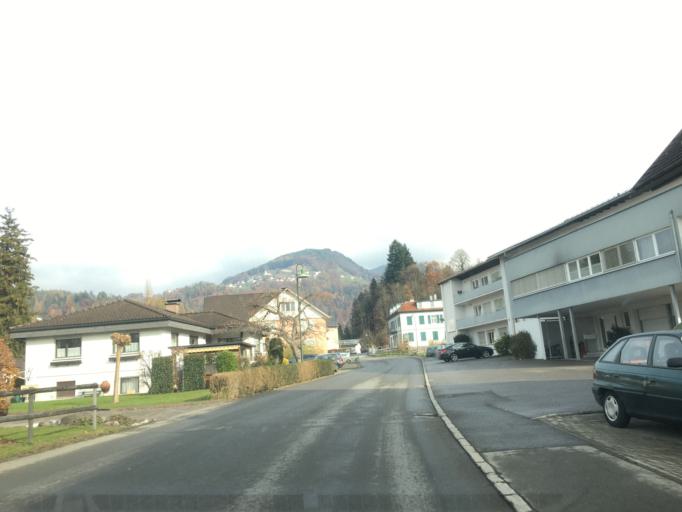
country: AT
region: Vorarlberg
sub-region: Politischer Bezirk Feldkirch
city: Rothis
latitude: 47.2865
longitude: 9.6615
